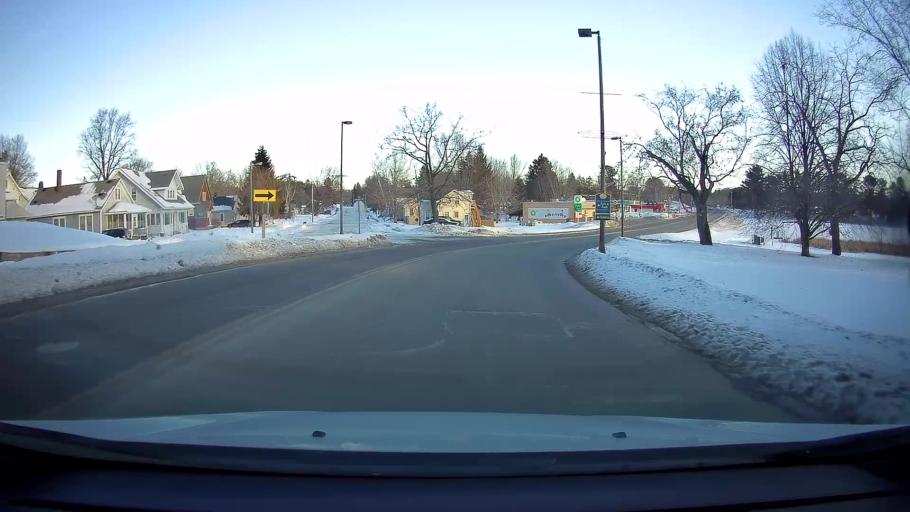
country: US
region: Wisconsin
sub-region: Barron County
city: Cumberland
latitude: 45.5397
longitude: -92.0219
